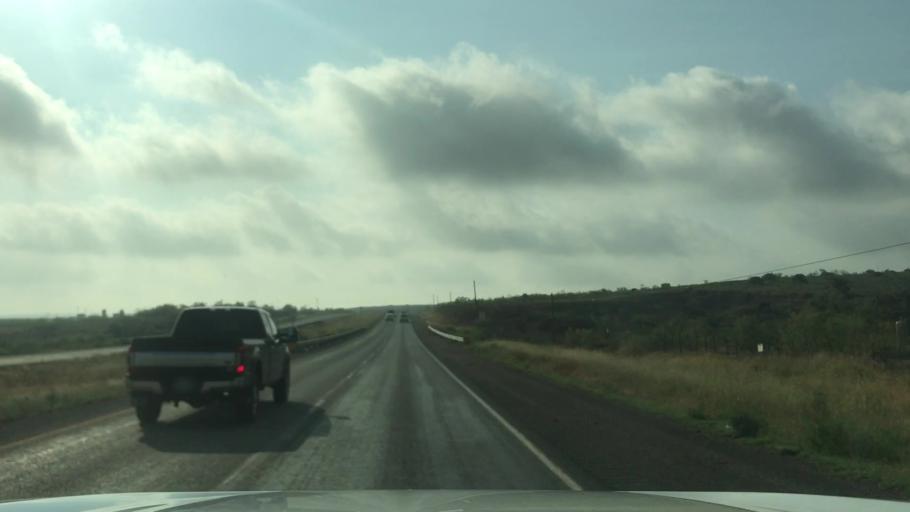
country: US
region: Texas
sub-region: Garza County
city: Post
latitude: 33.1768
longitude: -101.3673
